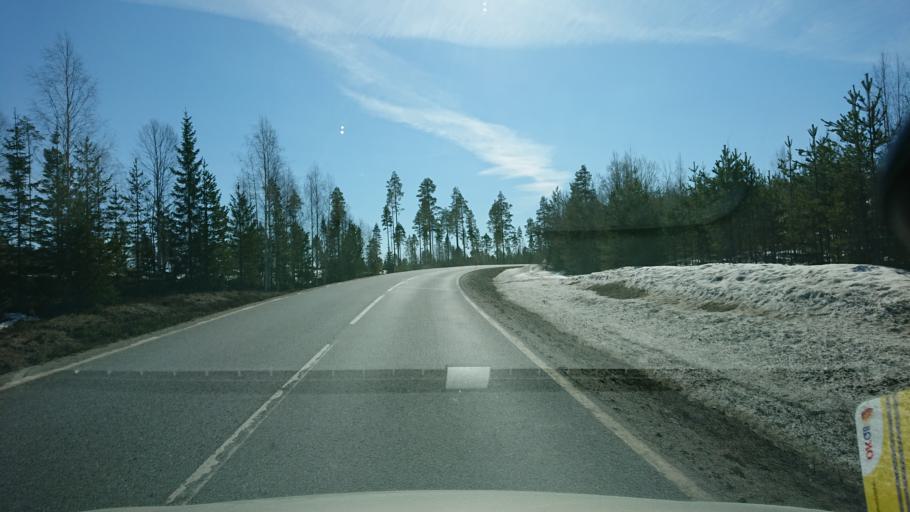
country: SE
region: Vaesterbotten
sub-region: Dorotea Kommun
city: Dorotea
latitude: 64.0199
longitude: 16.2879
